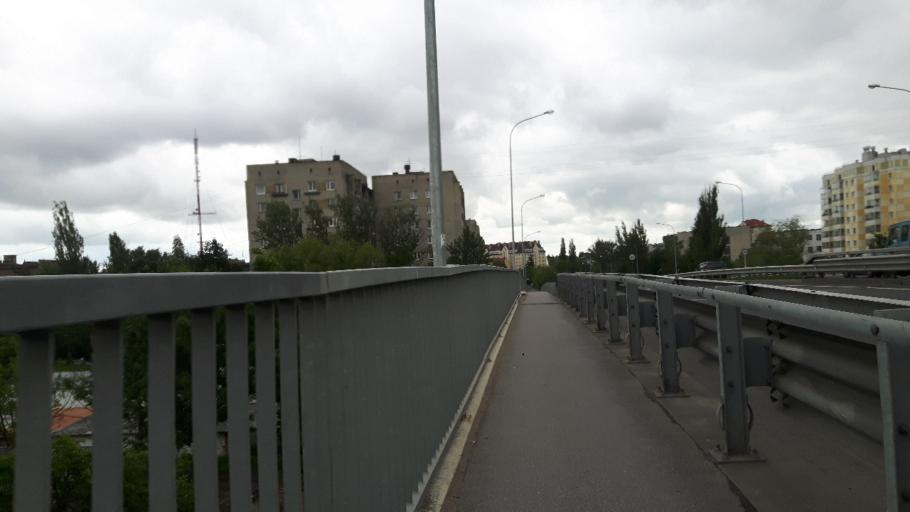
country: RU
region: Kaliningrad
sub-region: Gorod Kaliningrad
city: Kaliningrad
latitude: 54.7350
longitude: 20.4927
